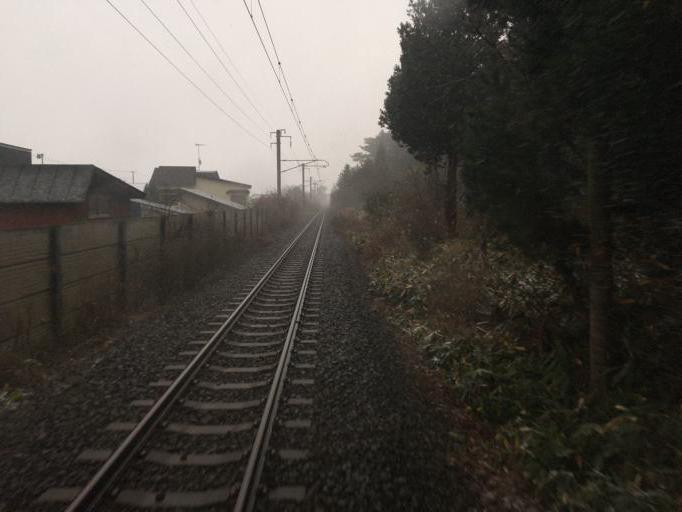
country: JP
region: Aomori
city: Aomori Shi
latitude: 40.9980
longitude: 140.6511
